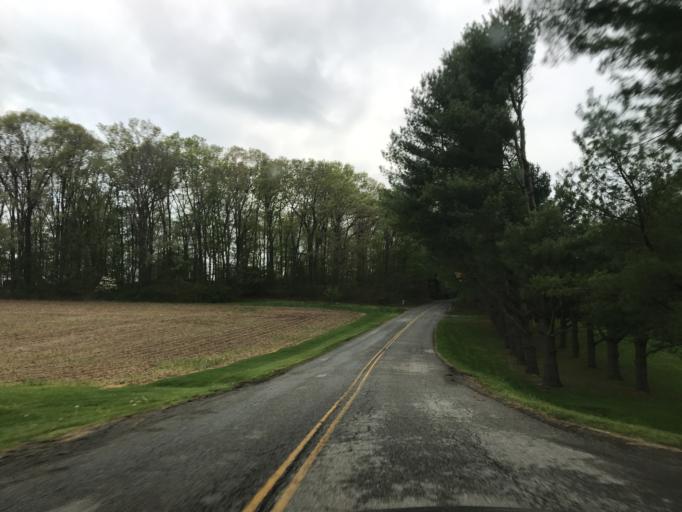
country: US
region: Maryland
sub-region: Harford County
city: Jarrettsville
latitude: 39.6669
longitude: -76.4832
